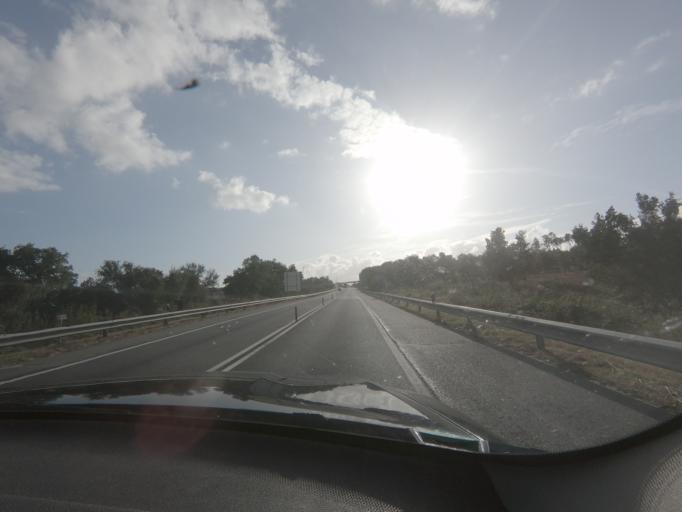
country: PT
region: Viseu
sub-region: Concelho de Tondela
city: Tondela
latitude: 40.5280
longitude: -8.0764
